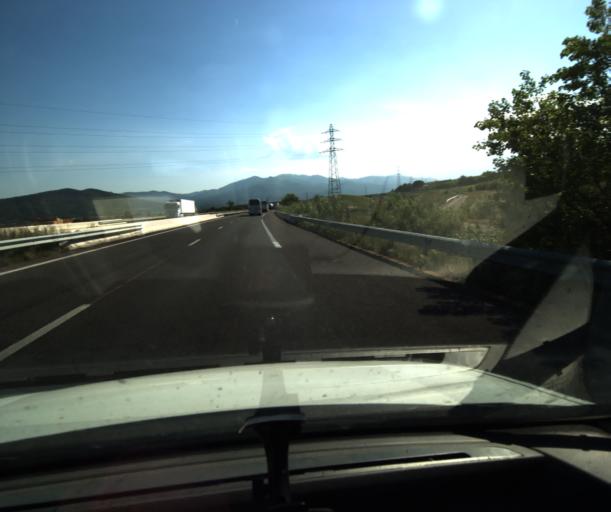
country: FR
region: Languedoc-Roussillon
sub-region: Departement des Pyrenees-Orientales
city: el Volo
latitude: 42.5439
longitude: 2.8473
